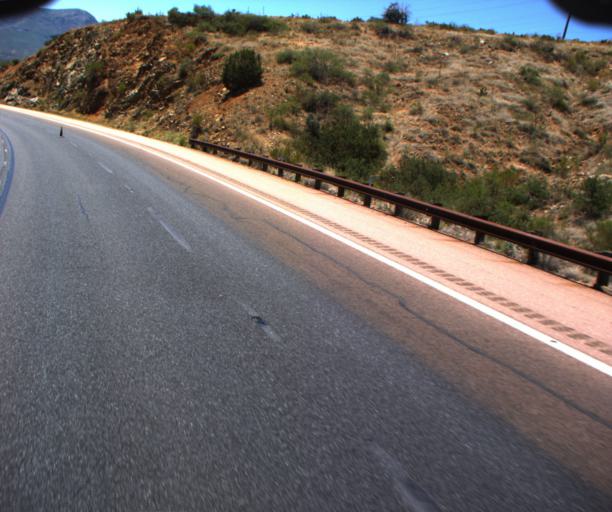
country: US
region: Arizona
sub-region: Gila County
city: Payson
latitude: 34.1539
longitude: -111.3468
